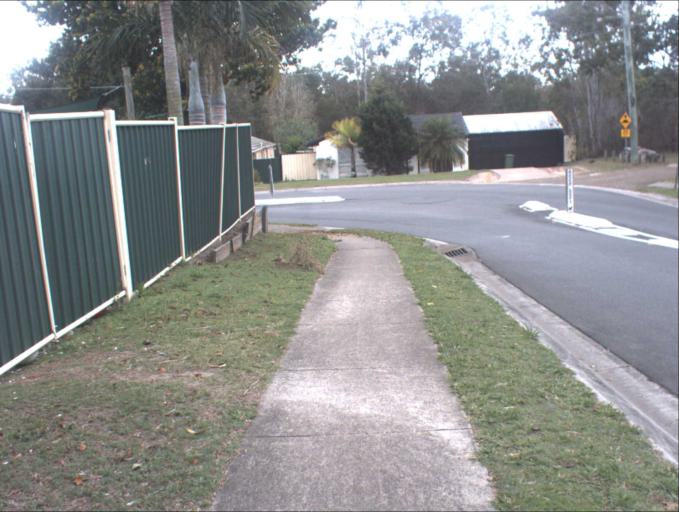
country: AU
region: Queensland
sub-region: Logan
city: Park Ridge South
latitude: -27.6930
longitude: 153.0248
